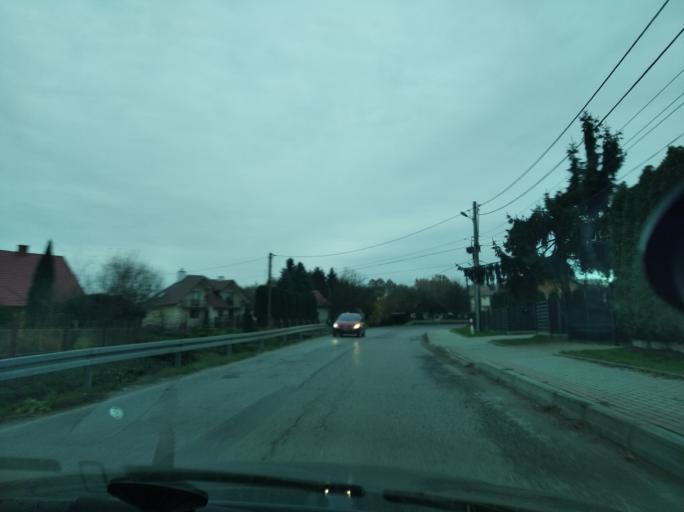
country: PL
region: Subcarpathian Voivodeship
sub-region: Powiat lancucki
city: Krzemienica
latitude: 50.0792
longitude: 22.1902
